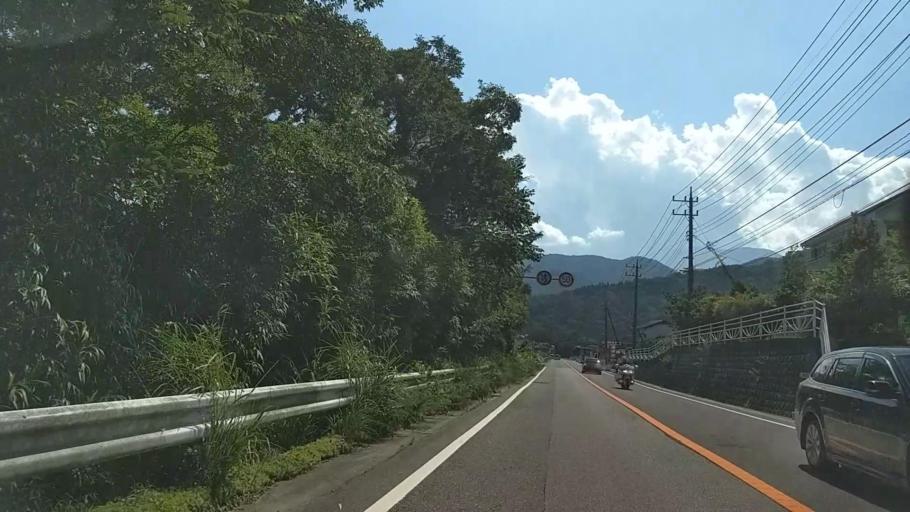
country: JP
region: Yamanashi
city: Ryuo
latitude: 35.4434
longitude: 138.4396
